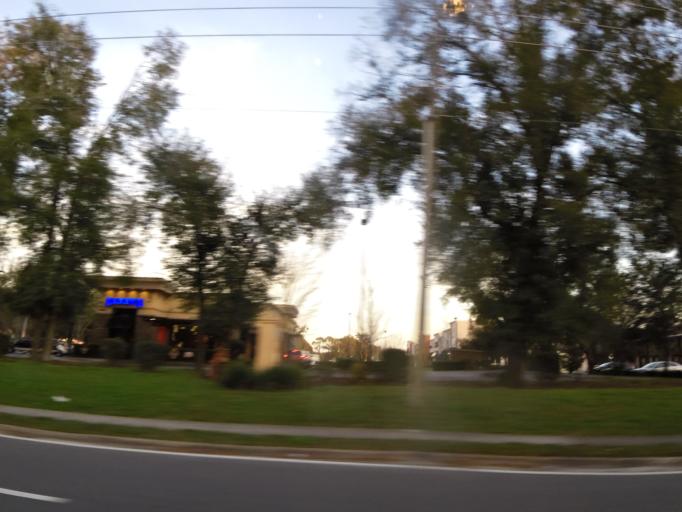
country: US
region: Florida
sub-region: Volusia County
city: North DeLand
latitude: 29.0597
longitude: -81.3044
